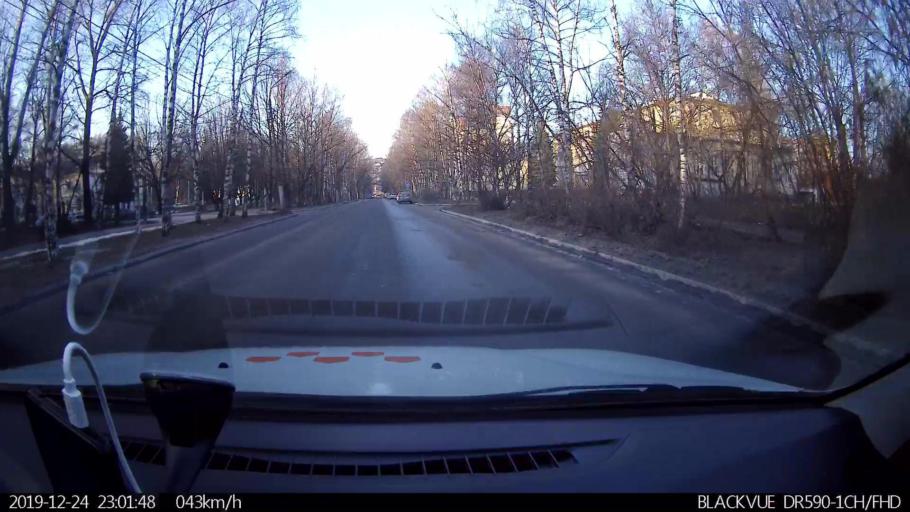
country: RU
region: Nizjnij Novgorod
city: Nizhniy Novgorod
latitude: 56.2685
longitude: 43.9243
